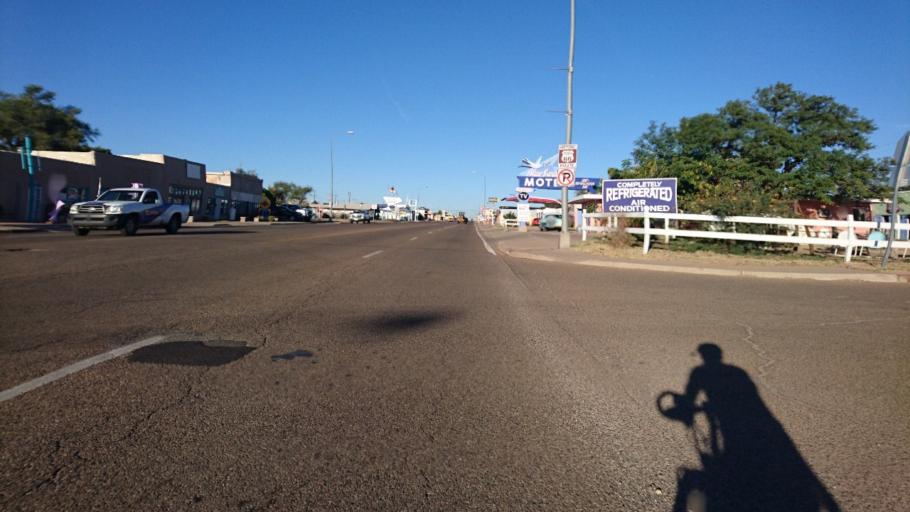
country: US
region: New Mexico
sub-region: Quay County
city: Tucumcari
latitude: 35.1719
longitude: -103.7159
